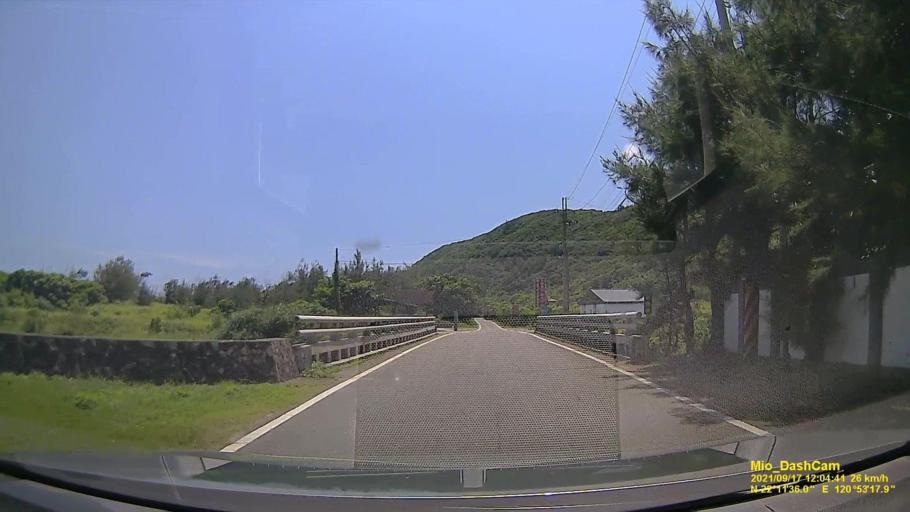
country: TW
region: Taiwan
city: Hengchun
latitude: 22.1934
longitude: 120.8883
